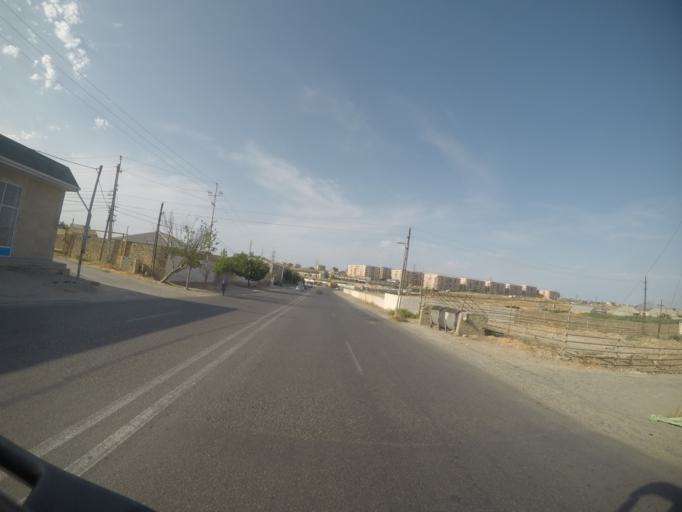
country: AZ
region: Baki
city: Binagadi
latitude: 40.4787
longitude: 49.8342
